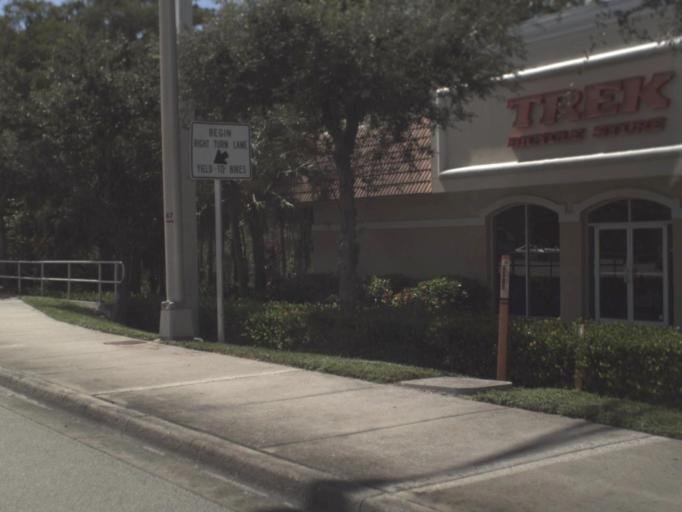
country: US
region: Florida
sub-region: Collier County
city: Naples Park
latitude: 26.2541
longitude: -81.8014
